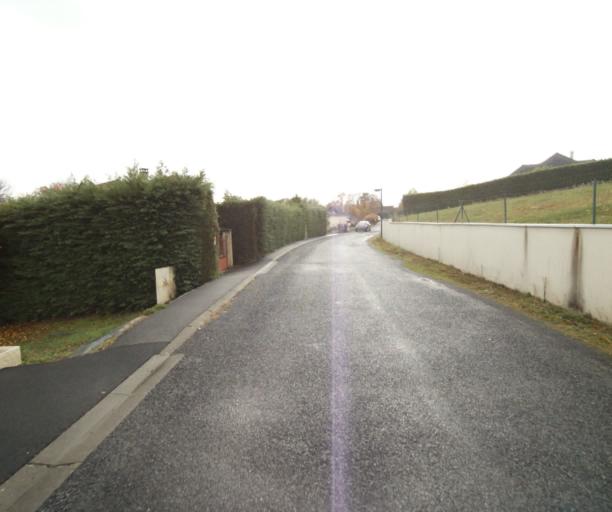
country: FR
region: Limousin
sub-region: Departement de la Correze
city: Cornil
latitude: 45.2204
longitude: 1.6448
